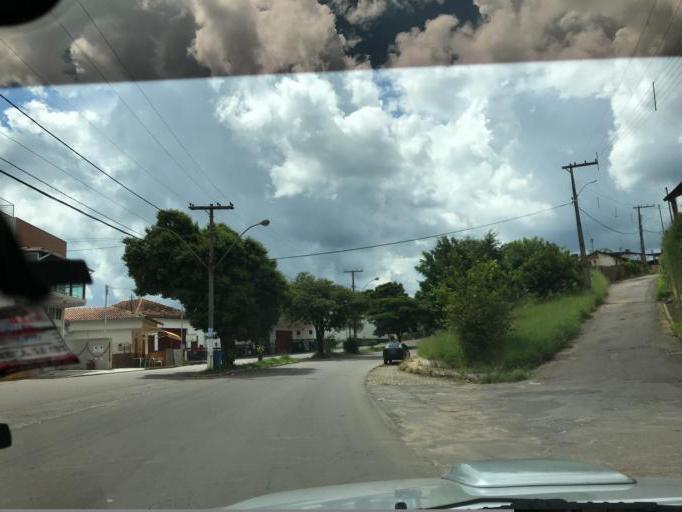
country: BR
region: Minas Gerais
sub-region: Cambuquira
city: Cambuquira
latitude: -21.8457
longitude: -45.2972
